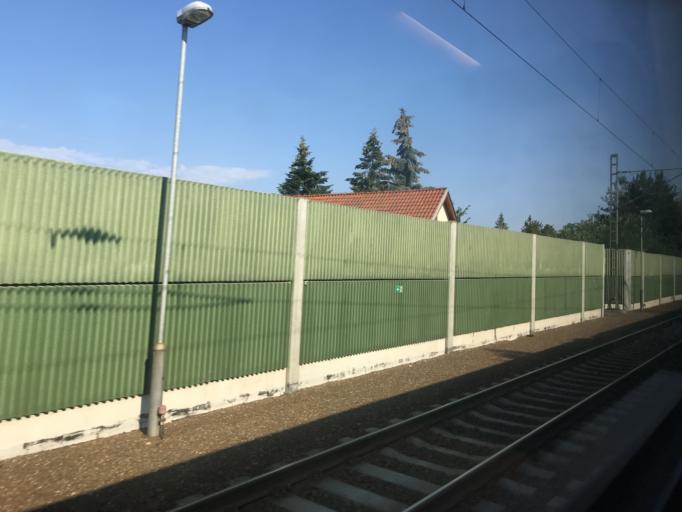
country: CZ
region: Jihocesky
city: Plana nad Luznici
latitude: 49.3476
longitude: 14.7089
